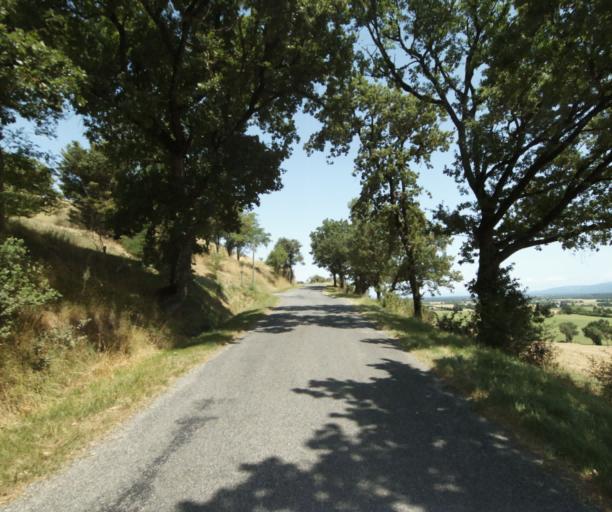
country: FR
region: Midi-Pyrenees
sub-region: Departement de la Haute-Garonne
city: Saint-Felix-Lauragais
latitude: 43.4380
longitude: 1.8955
